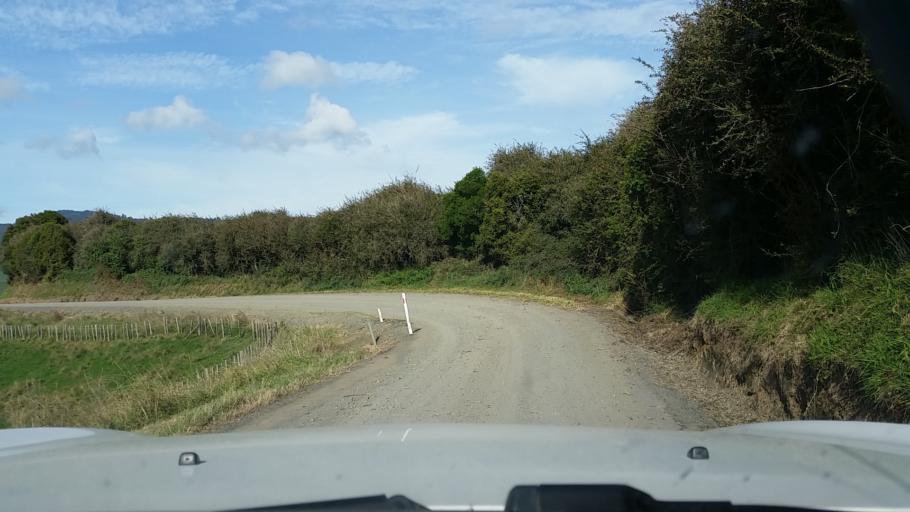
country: NZ
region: Waikato
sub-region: Matamata-Piako District
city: Matamata
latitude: -37.8016
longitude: 175.6326
